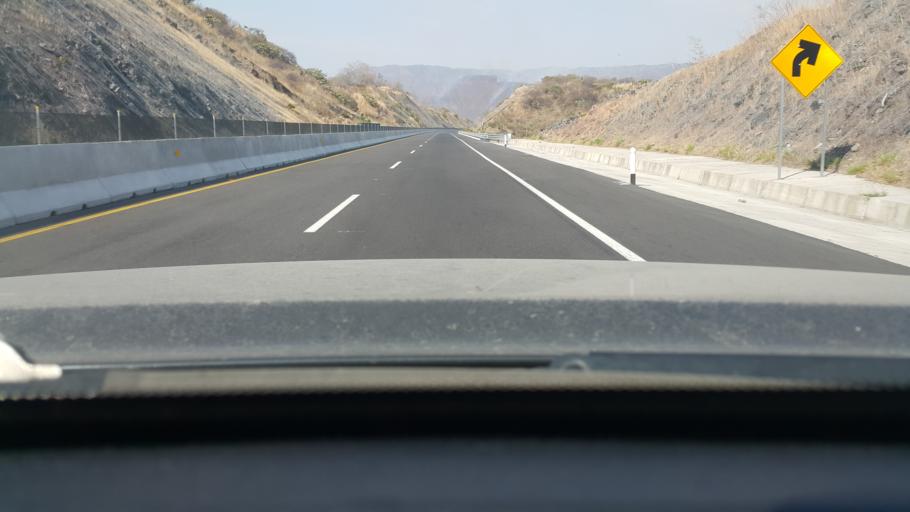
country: MX
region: Nayarit
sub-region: Ahuacatlan
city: Ahuacatlan
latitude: 21.0714
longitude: -104.4571
